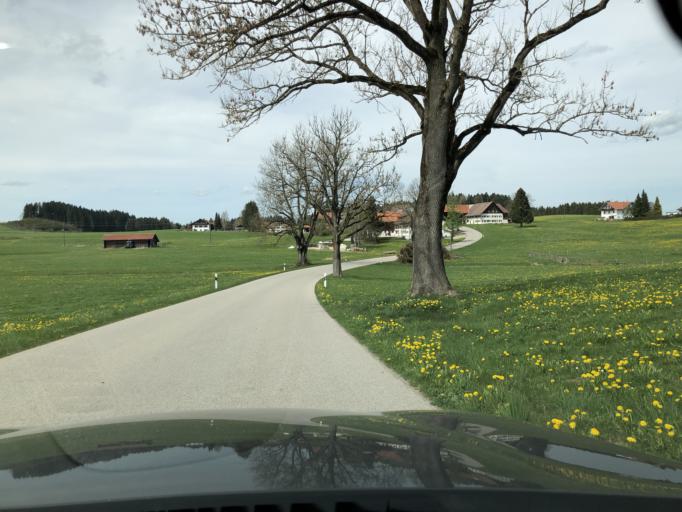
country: DE
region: Bavaria
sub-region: Swabia
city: Wald
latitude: 47.7048
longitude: 10.5574
